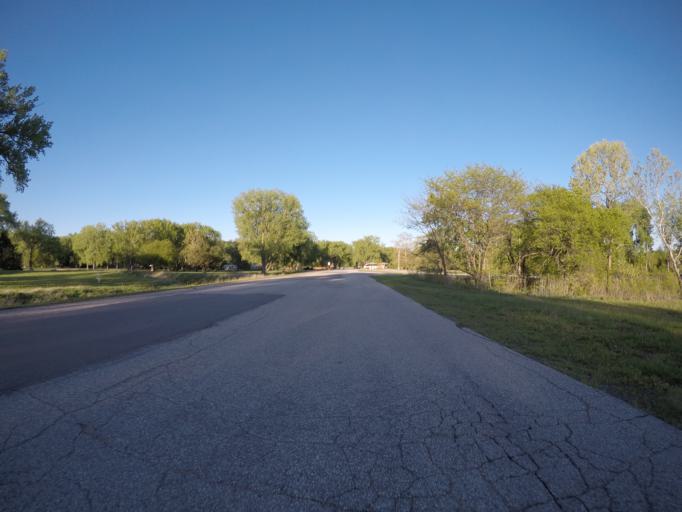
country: US
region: Kansas
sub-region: Riley County
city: Manhattan
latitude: 39.2555
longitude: -96.5821
